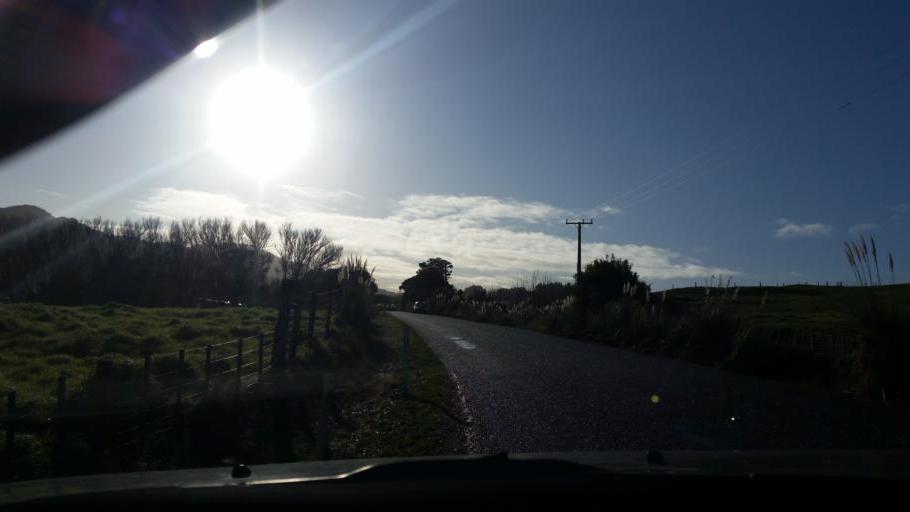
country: NZ
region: Auckland
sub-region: Auckland
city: Wellsford
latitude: -36.1224
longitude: 174.4485
